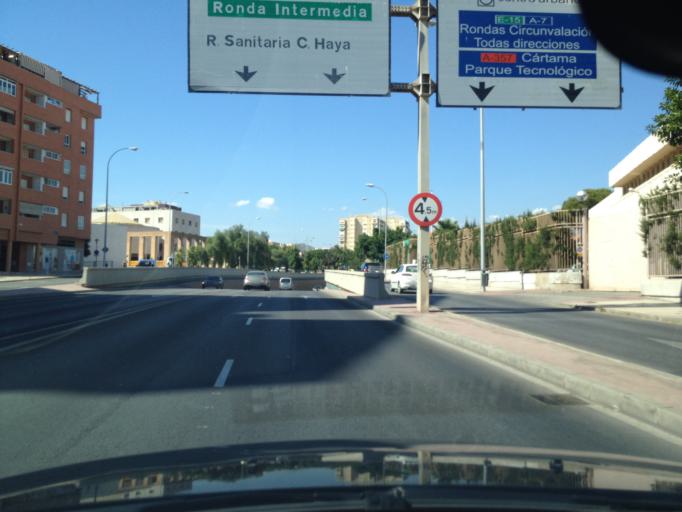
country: ES
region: Andalusia
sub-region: Provincia de Malaga
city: Malaga
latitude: 36.7128
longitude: -4.4469
